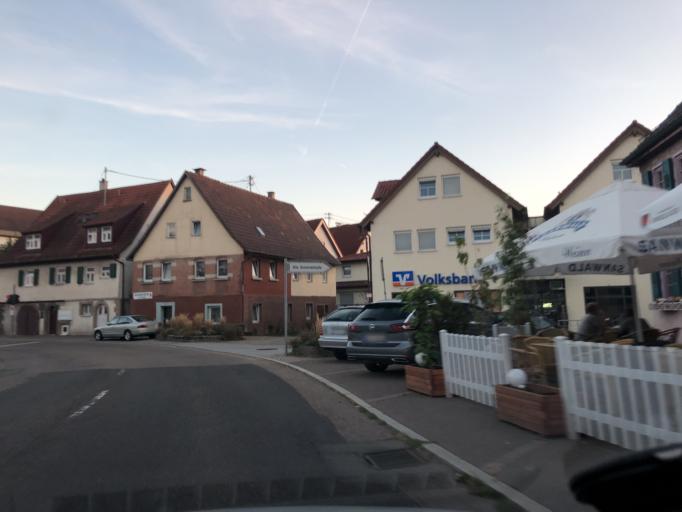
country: DE
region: Baden-Wuerttemberg
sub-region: Regierungsbezirk Stuttgart
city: Erdmannhausen
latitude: 48.8889
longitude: 9.2761
